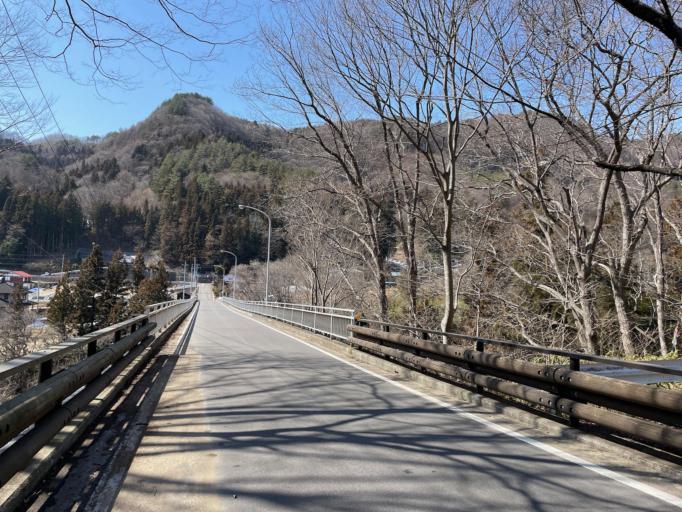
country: JP
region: Gunma
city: Nakanojomachi
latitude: 36.5779
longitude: 138.6259
